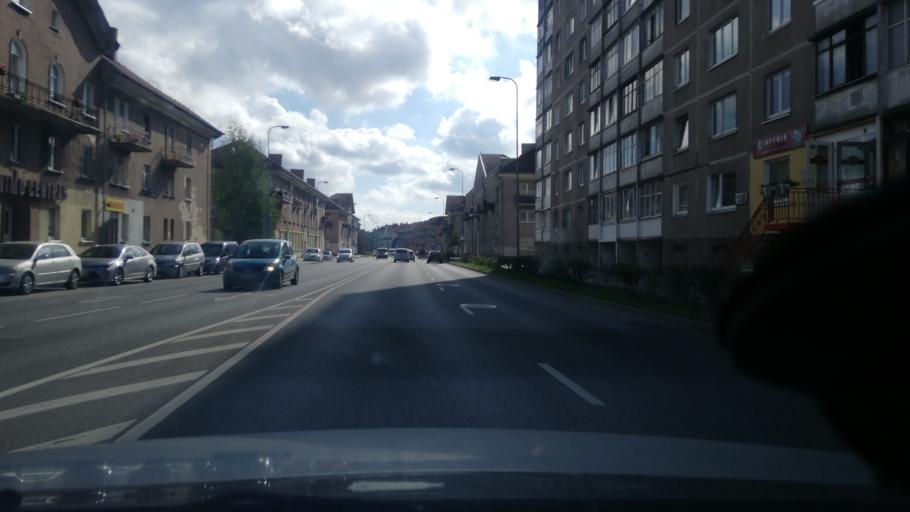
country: LT
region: Klaipedos apskritis
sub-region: Klaipeda
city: Klaipeda
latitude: 55.6804
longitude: 21.1514
